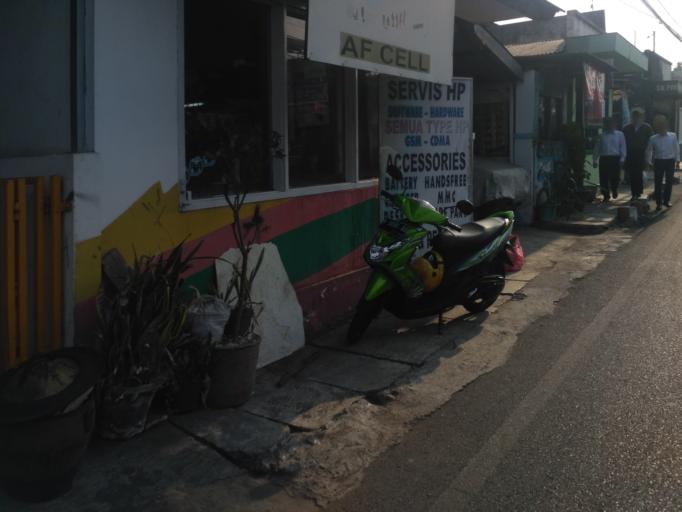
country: ID
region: East Java
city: Malang
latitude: -7.9641
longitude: 112.6341
